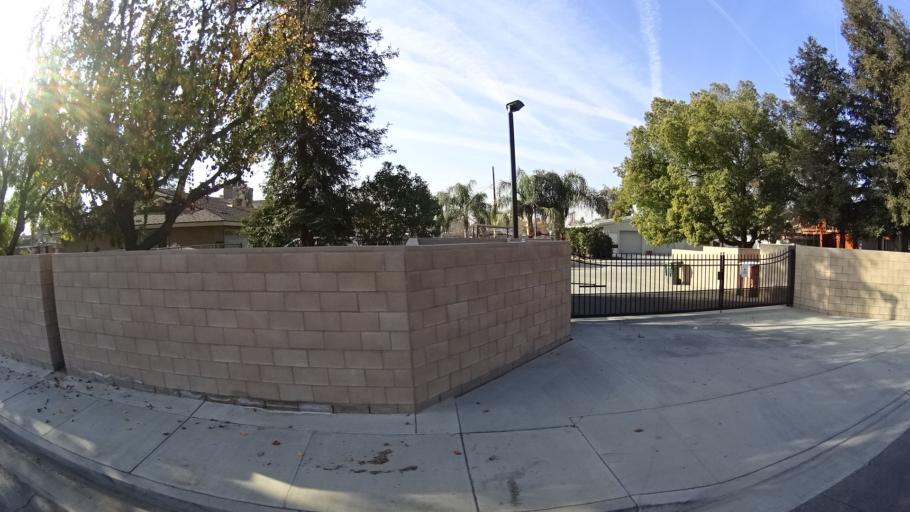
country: US
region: California
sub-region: Kern County
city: Bakersfield
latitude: 35.3216
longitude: -119.0321
